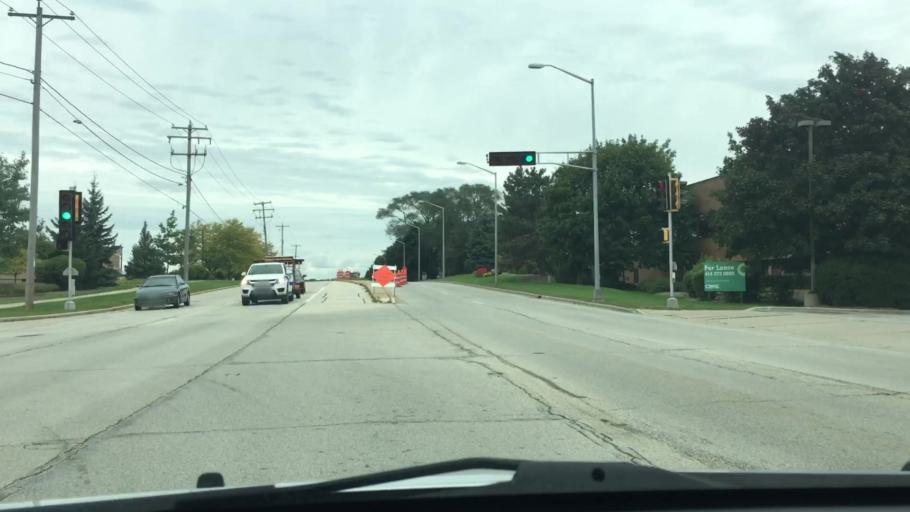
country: US
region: Wisconsin
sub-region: Waukesha County
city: Waukesha
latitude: 43.0395
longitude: -88.2559
